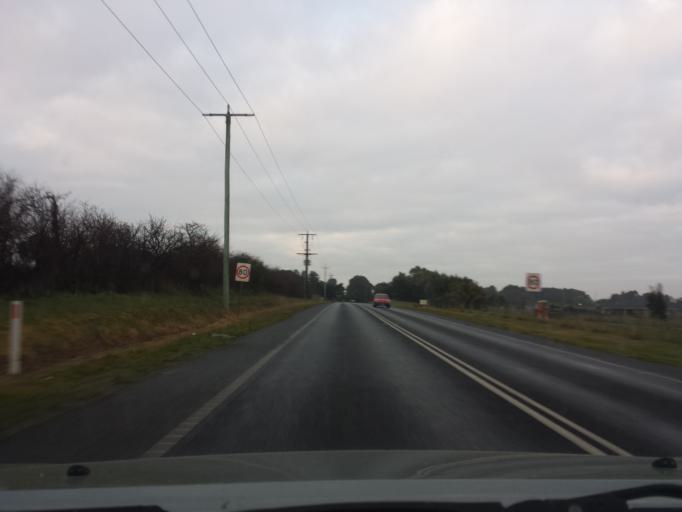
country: AU
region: Victoria
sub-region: Casey
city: Narre Warren North
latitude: -37.9737
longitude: 145.3155
